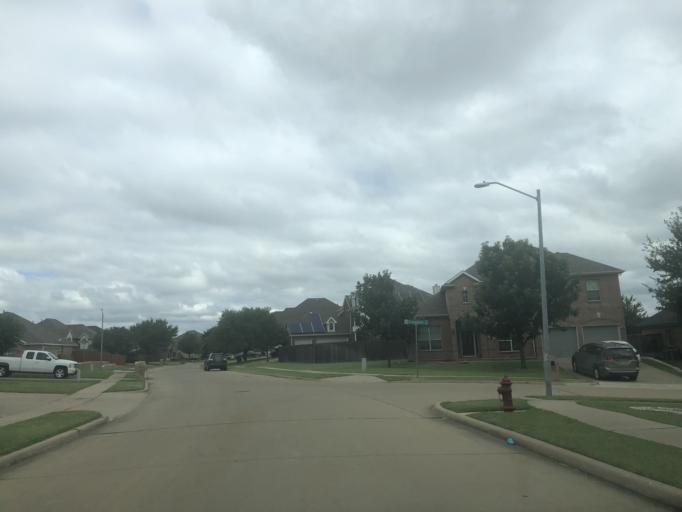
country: US
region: Texas
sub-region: Dallas County
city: Cedar Hill
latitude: 32.6558
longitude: -96.9991
